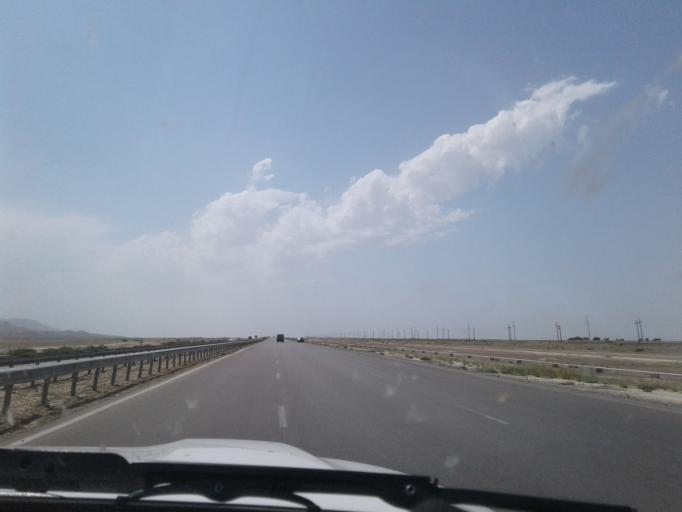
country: IR
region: Razavi Khorasan
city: Dargaz
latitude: 37.7472
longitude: 58.9619
